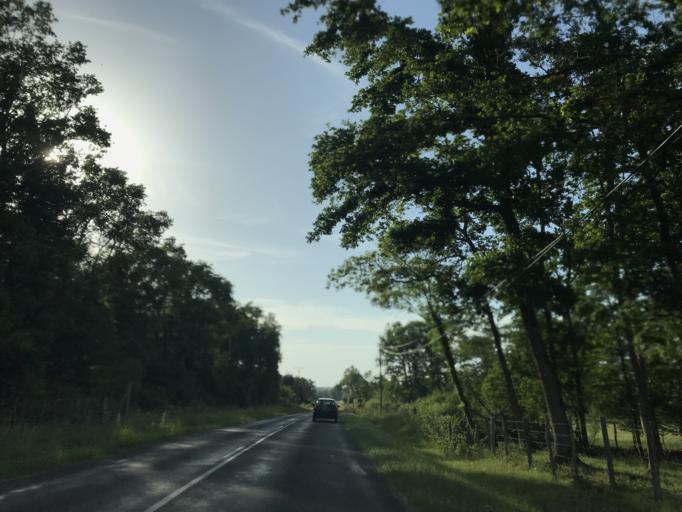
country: FR
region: Auvergne
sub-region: Departement du Puy-de-Dome
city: Lezoux
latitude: 45.8090
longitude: 3.4030
